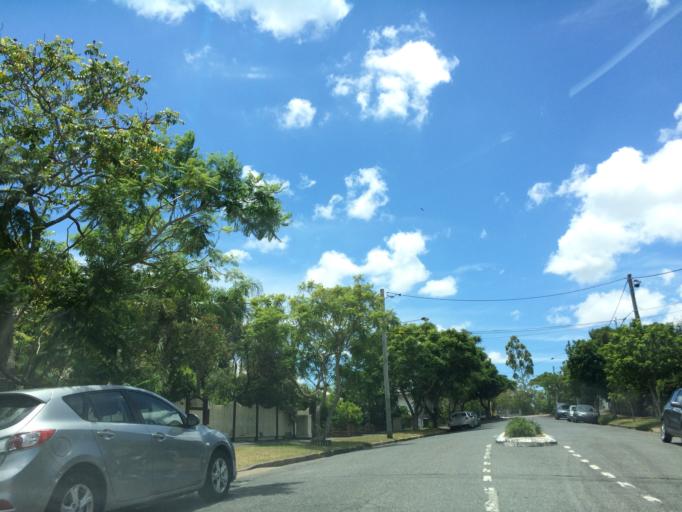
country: AU
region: Queensland
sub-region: Brisbane
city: South Brisbane
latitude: -27.4881
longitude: 153.0066
